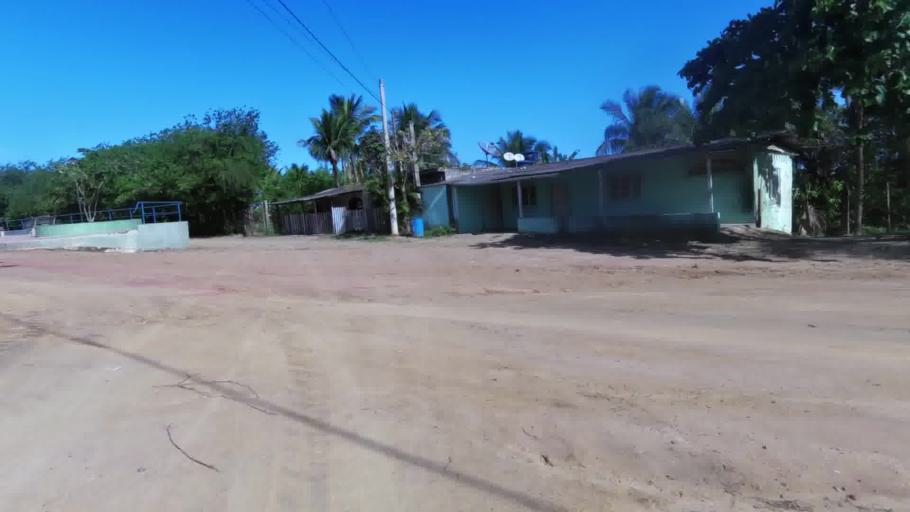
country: BR
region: Espirito Santo
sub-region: Piuma
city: Piuma
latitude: -20.8240
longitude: -40.6251
